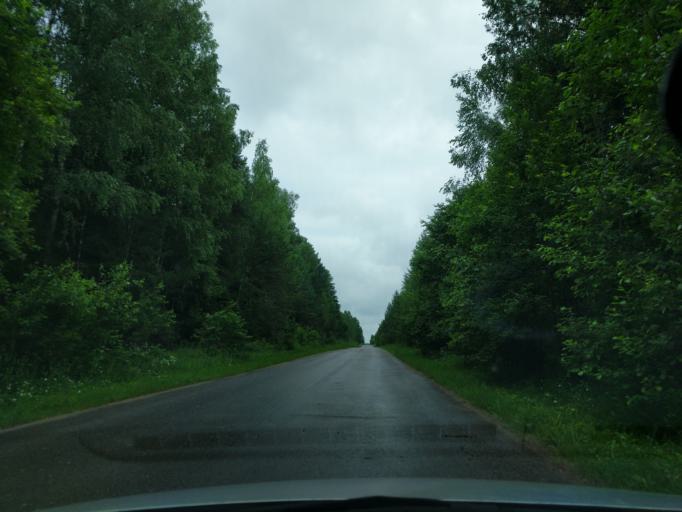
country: RU
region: Kaluga
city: Myatlevo
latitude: 54.8238
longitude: 35.6726
